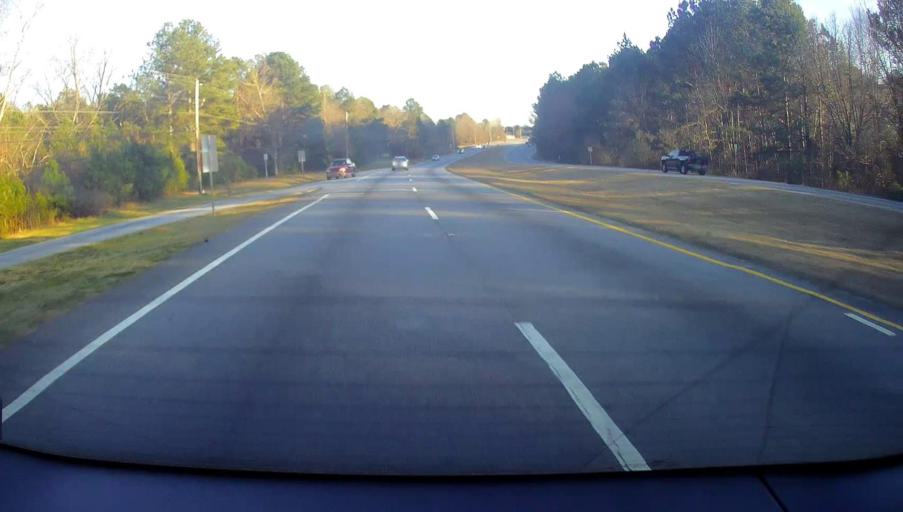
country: US
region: Georgia
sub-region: Fulton County
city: Fairburn
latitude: 33.5516
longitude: -84.5802
